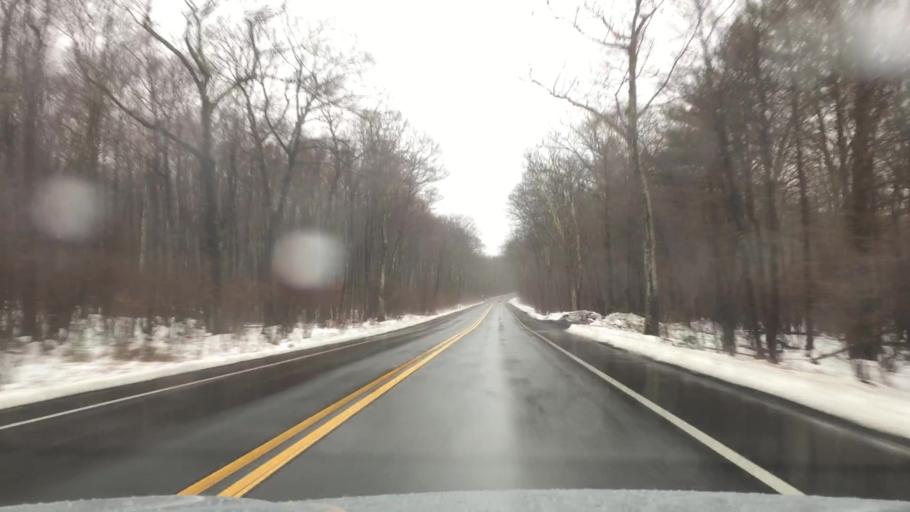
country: US
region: Massachusetts
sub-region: Hampshire County
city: Pelham
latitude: 42.4075
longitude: -72.4029
